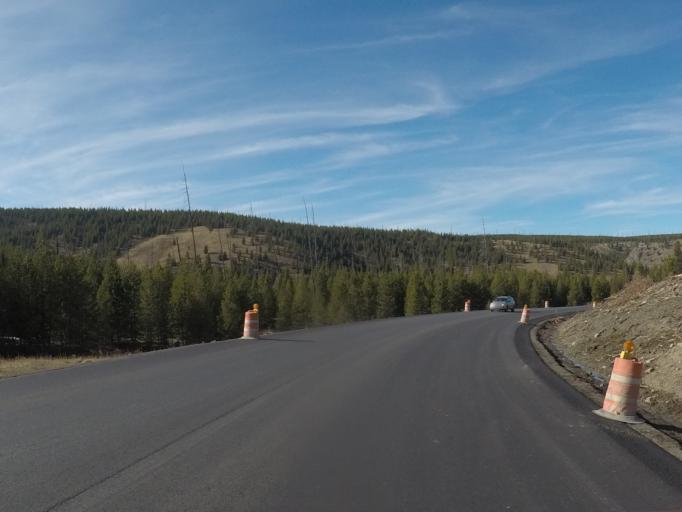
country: US
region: Montana
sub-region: Gallatin County
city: West Yellowstone
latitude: 44.7966
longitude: -110.7435
